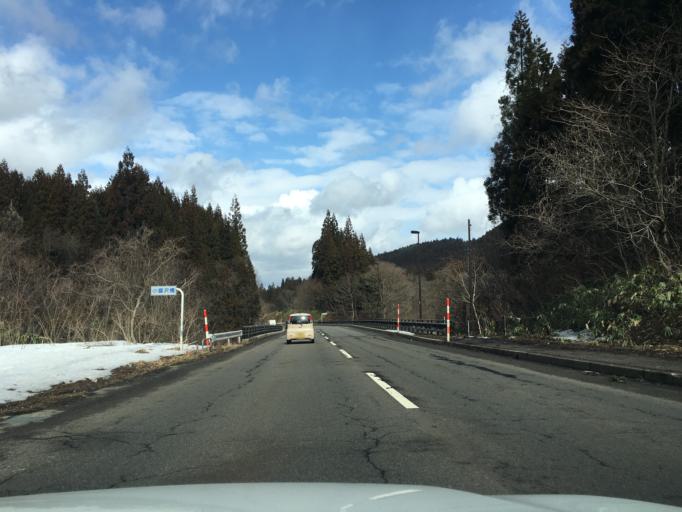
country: JP
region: Akita
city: Takanosu
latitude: 40.0117
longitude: 140.2788
